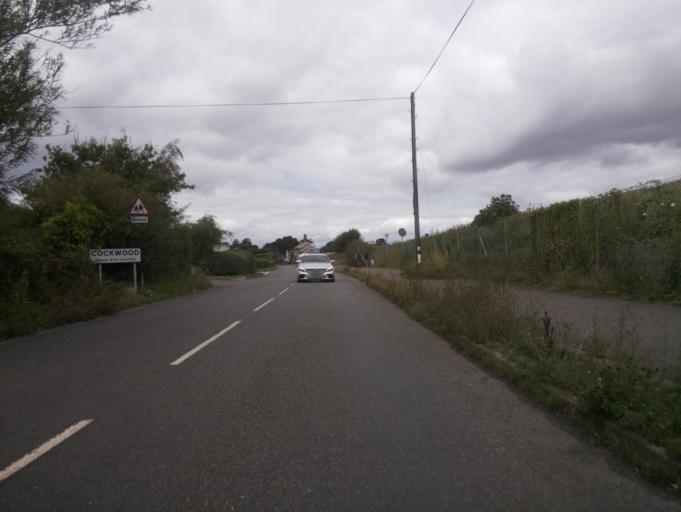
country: GB
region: England
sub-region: Devon
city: Starcross
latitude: 50.6148
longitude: -3.4463
